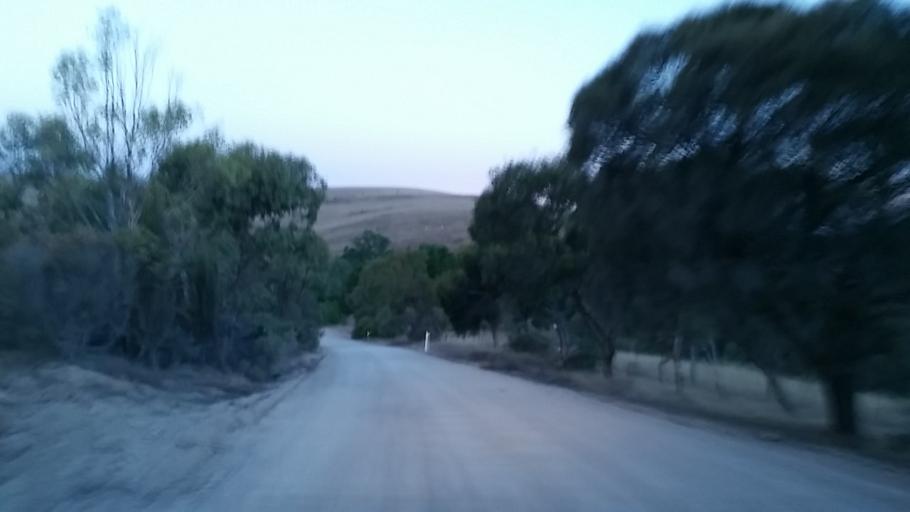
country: AU
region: South Australia
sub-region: Mount Barker
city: Callington
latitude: -35.0994
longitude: 138.9847
